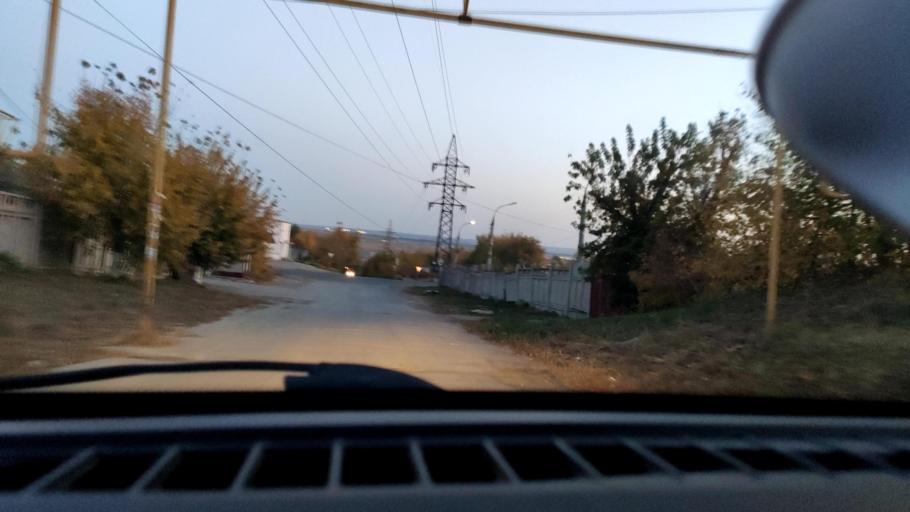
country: RU
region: Samara
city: Samara
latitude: 53.1830
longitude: 50.1715
